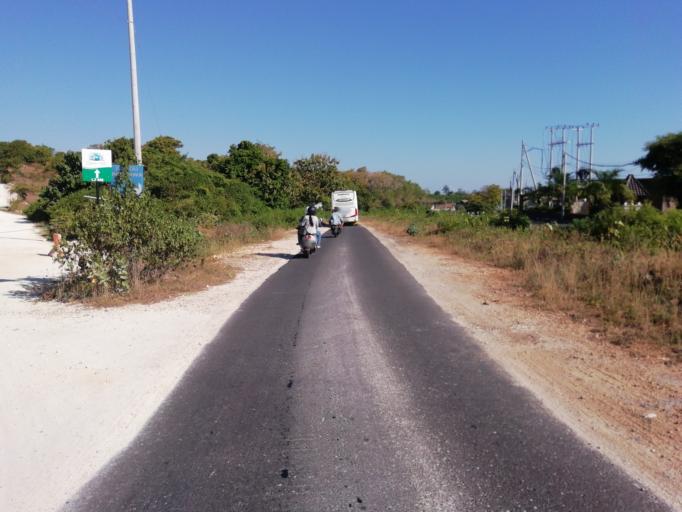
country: ID
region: Bali
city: Jimbaran
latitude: -8.8367
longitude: 115.1819
